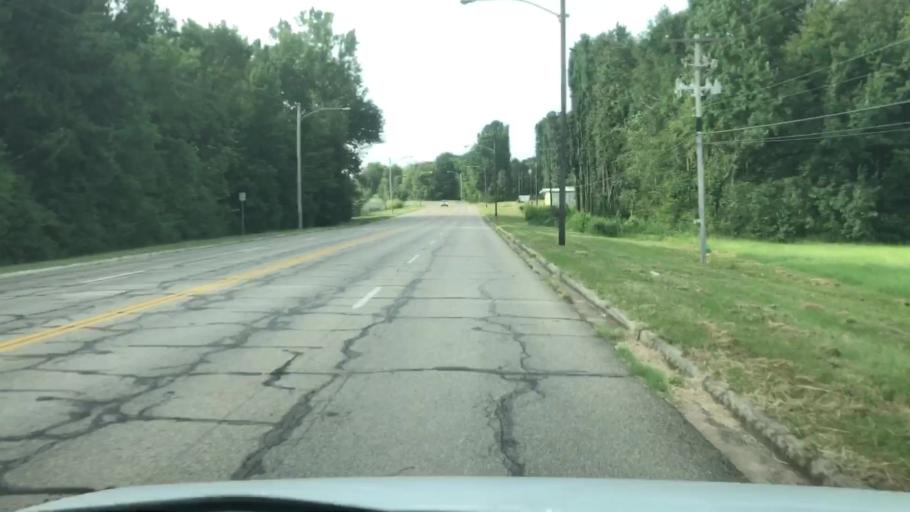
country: US
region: Texas
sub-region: Bowie County
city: Wake Village
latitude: 33.4116
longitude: -94.0804
